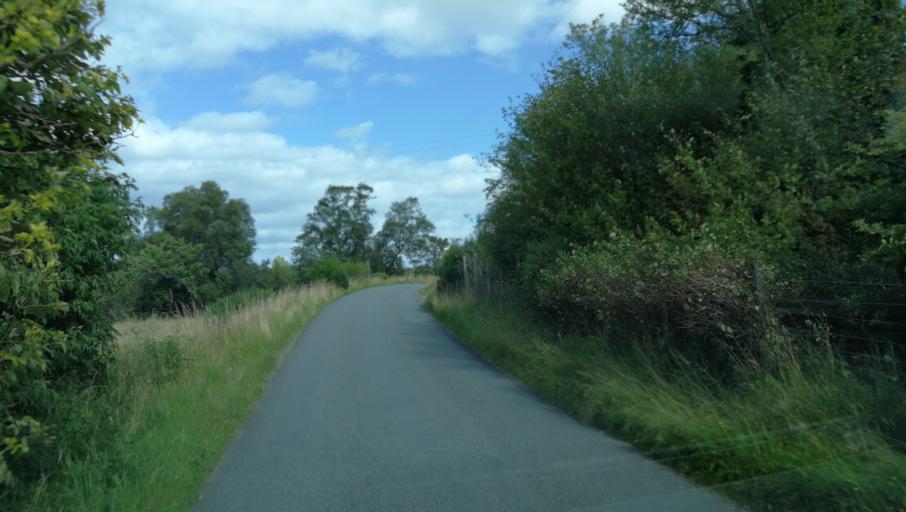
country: GB
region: Scotland
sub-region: Highland
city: Aviemore
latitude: 57.2189
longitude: -3.7621
